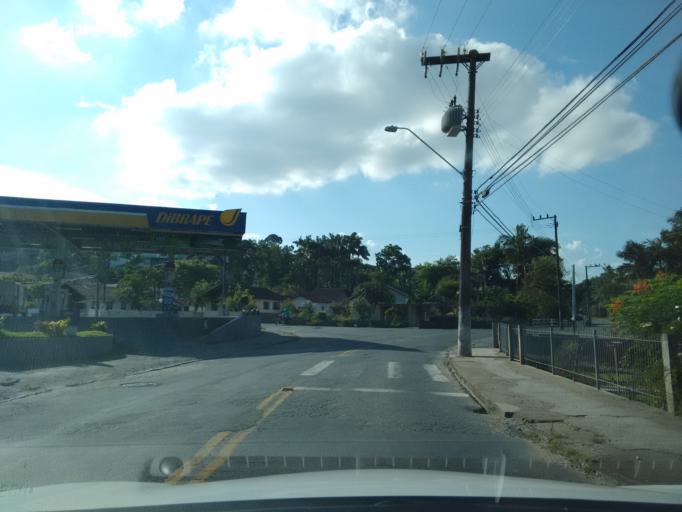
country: BR
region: Santa Catarina
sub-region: Blumenau
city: Blumenau
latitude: -26.8733
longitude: -49.0702
